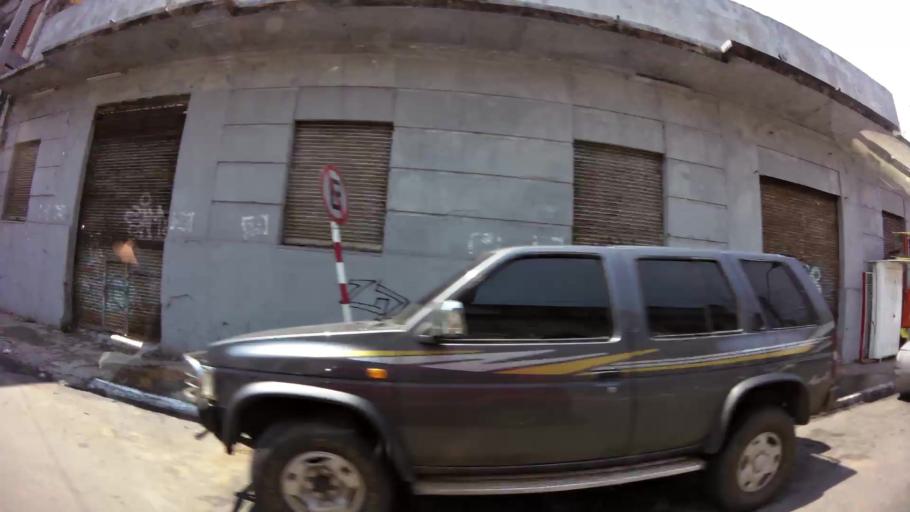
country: PY
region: Asuncion
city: Asuncion
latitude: -25.2782
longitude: -57.6394
